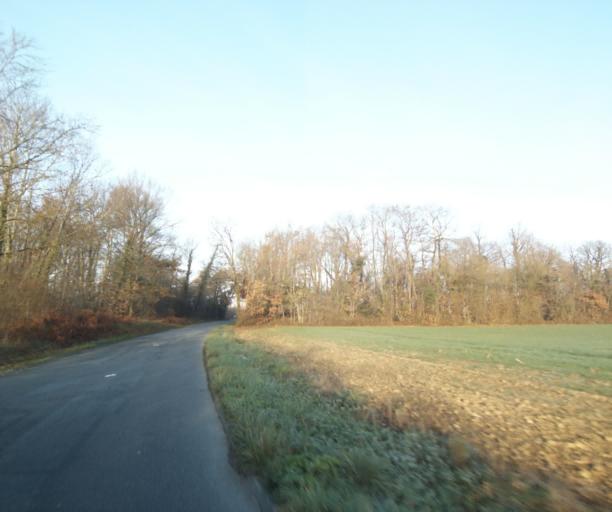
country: FR
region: Poitou-Charentes
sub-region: Departement de la Charente-Maritime
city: Fontcouverte
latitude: 45.7583
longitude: -0.5722
